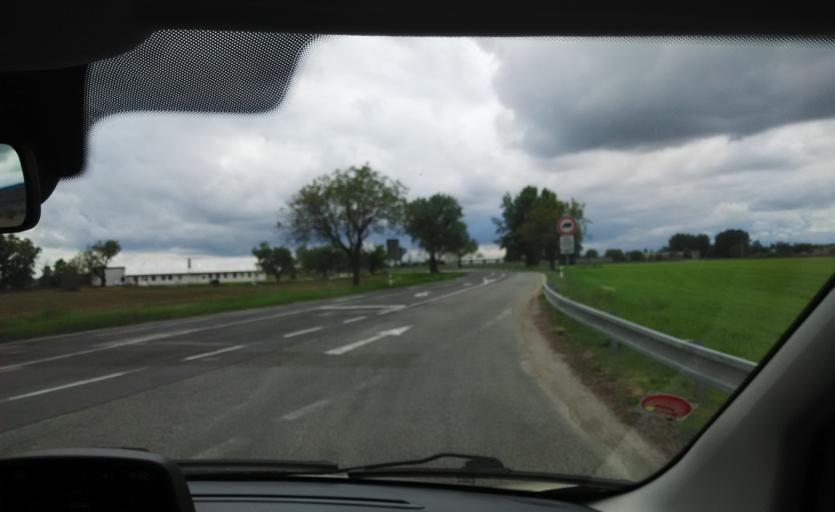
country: SK
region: Trnavsky
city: Leopoldov
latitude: 48.4669
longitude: 17.7666
